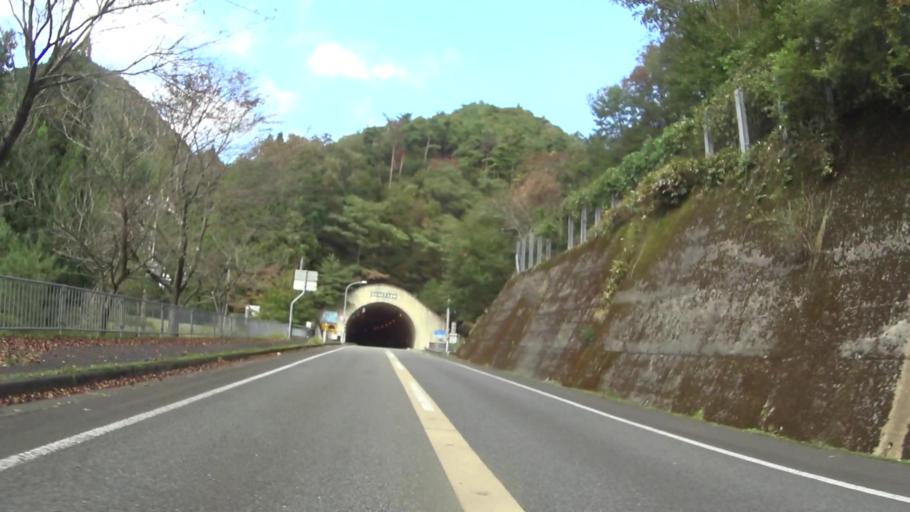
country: JP
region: Hyogo
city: Toyooka
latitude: 35.5234
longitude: 134.9874
